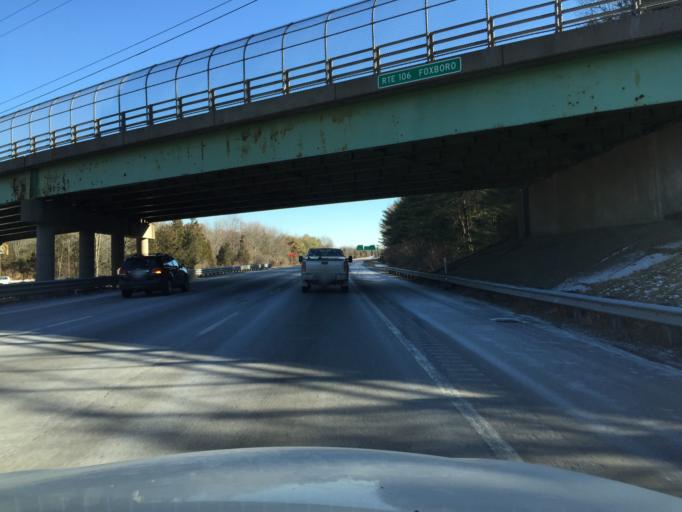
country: US
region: Massachusetts
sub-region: Norfolk County
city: Foxborough
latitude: 42.0299
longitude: -71.2658
